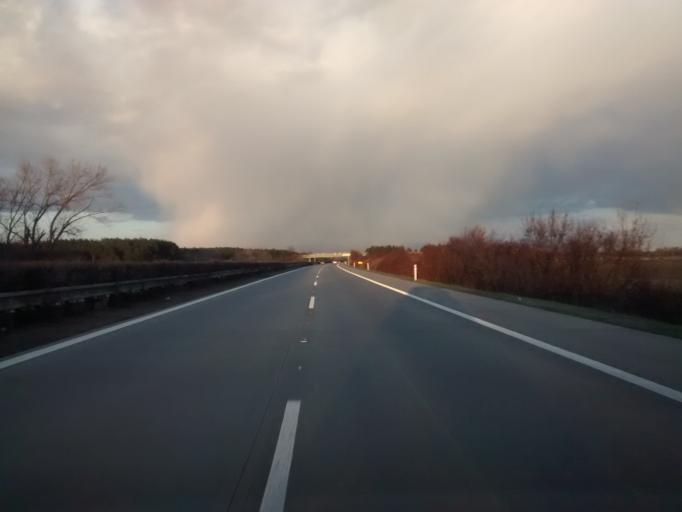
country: CZ
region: Central Bohemia
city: Pecky
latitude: 50.1236
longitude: 15.0210
